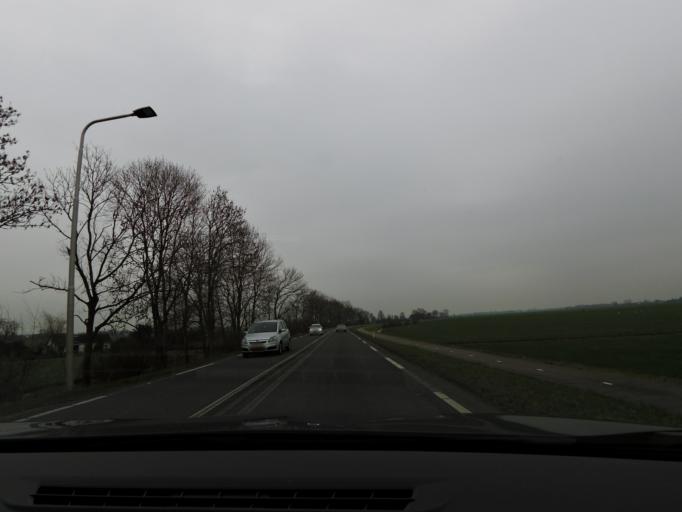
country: NL
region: Utrecht
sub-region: Gemeente De Ronde Venen
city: Mijdrecht
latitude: 52.1613
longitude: 4.9096
